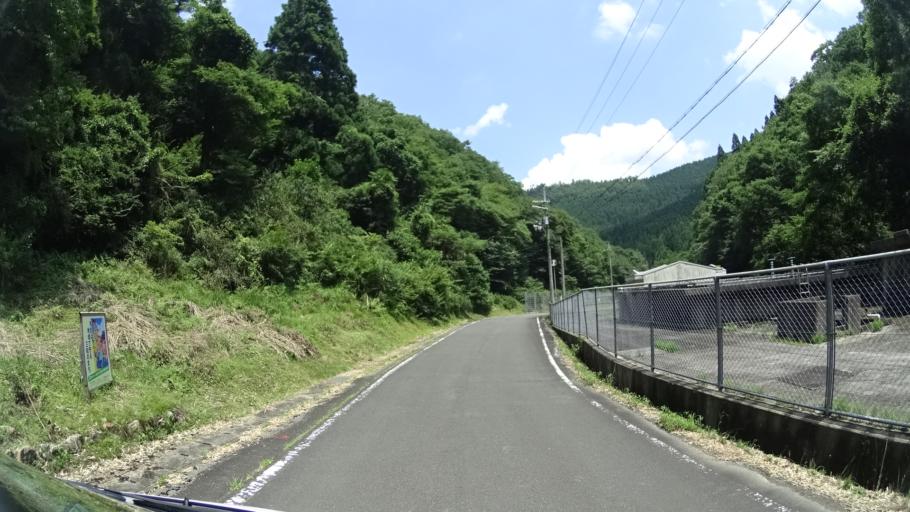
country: JP
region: Hyogo
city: Sasayama
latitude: 35.1782
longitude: 135.2166
